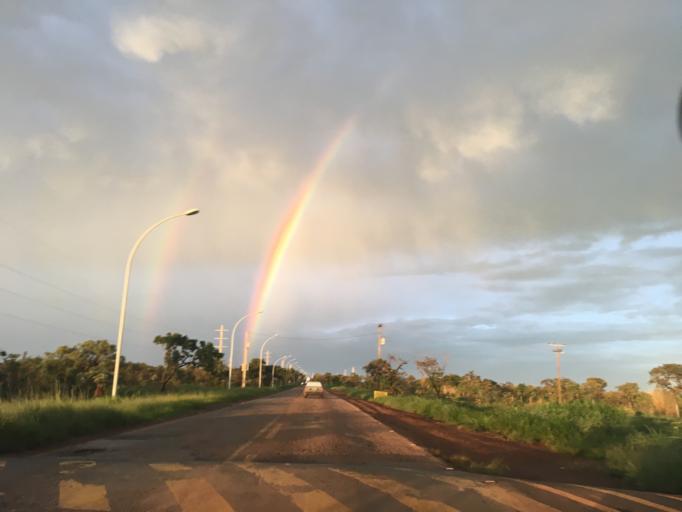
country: BR
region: Federal District
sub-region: Brasilia
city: Brasilia
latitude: -15.9747
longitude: -47.9790
